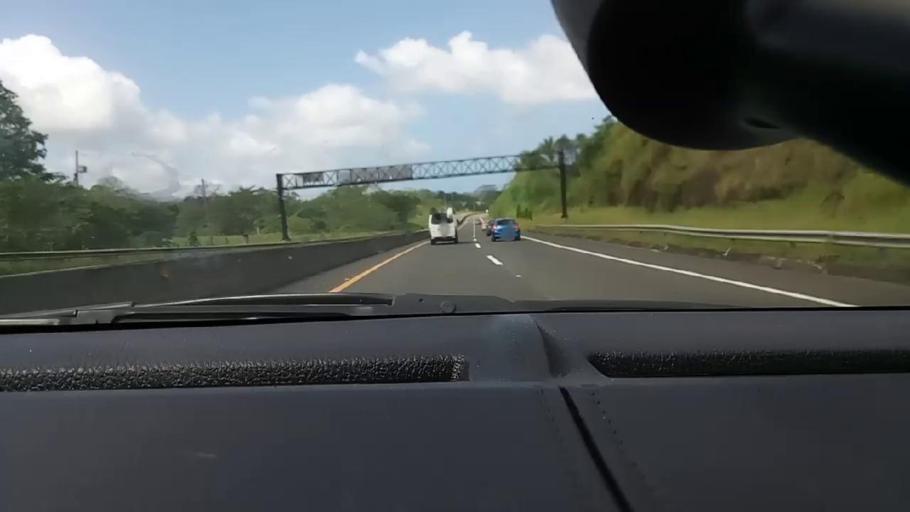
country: PA
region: Colon
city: Las Margaritas
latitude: 9.3280
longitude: -79.8690
